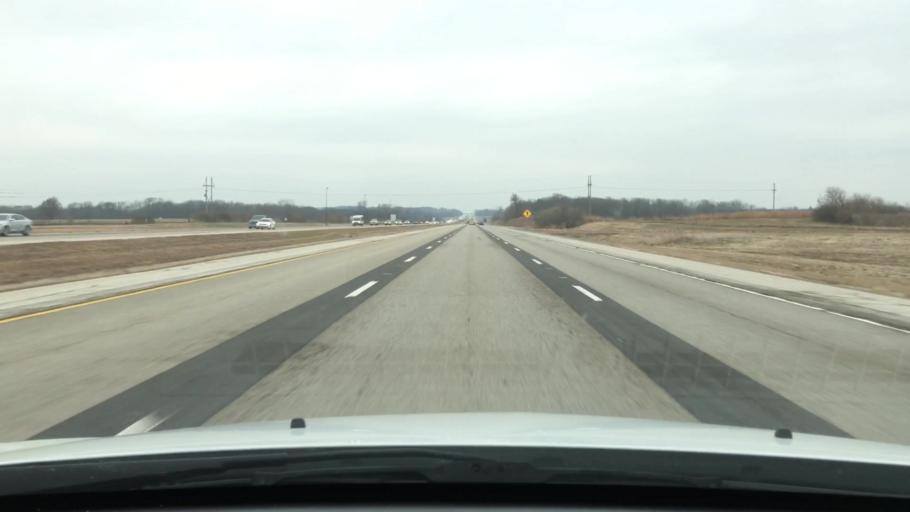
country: US
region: Illinois
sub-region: Logan County
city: Lincoln
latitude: 40.1141
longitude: -89.4163
